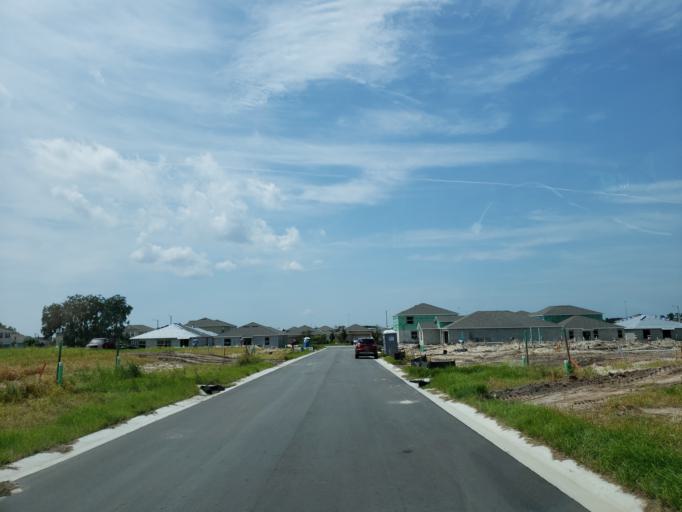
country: US
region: Florida
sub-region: Hillsborough County
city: Riverview
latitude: 27.8475
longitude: -82.3379
